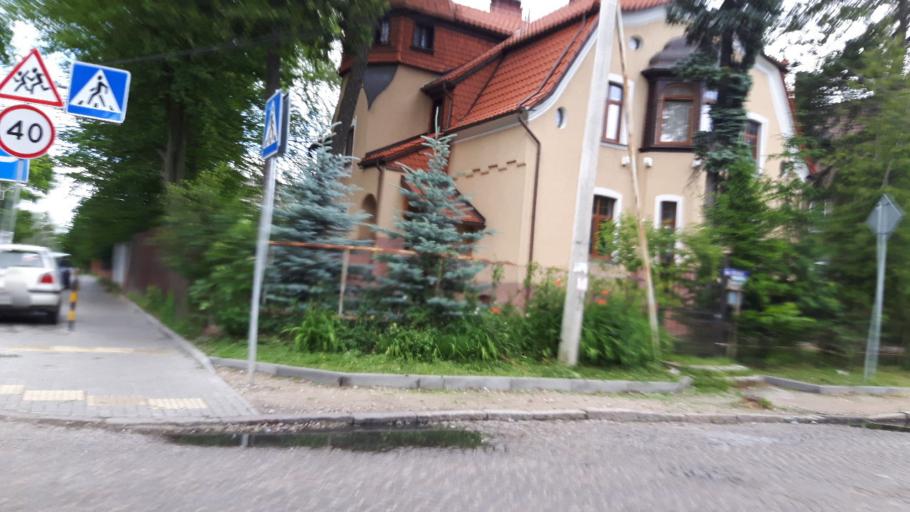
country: RU
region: Kaliningrad
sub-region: Gorod Kaliningrad
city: Kaliningrad
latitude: 54.7340
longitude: 20.5181
